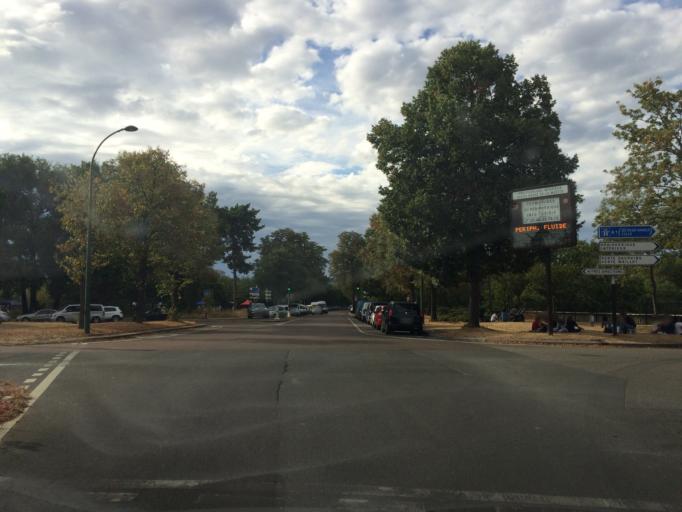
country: FR
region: Ile-de-France
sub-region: Departement des Hauts-de-Seine
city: Neuilly-sur-Seine
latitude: 48.8639
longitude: 2.2673
